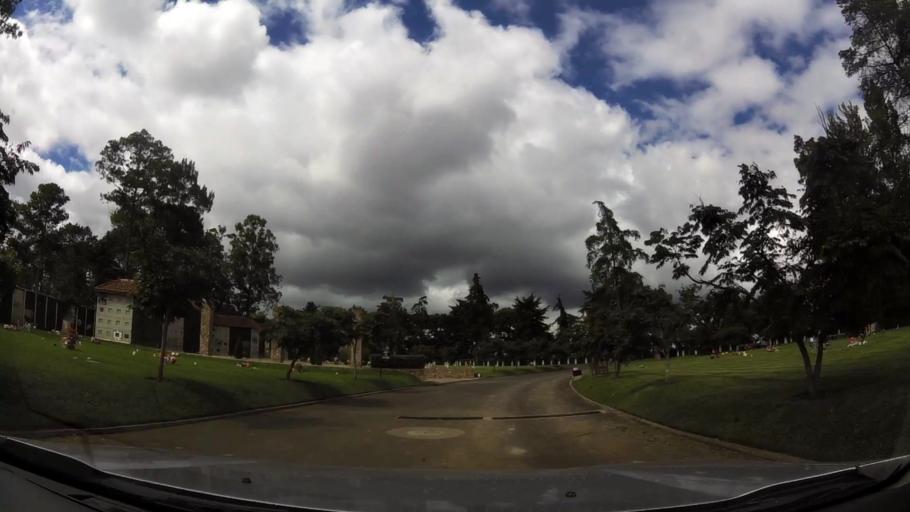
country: GT
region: Guatemala
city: Chinautla
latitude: 14.6874
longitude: -90.5418
